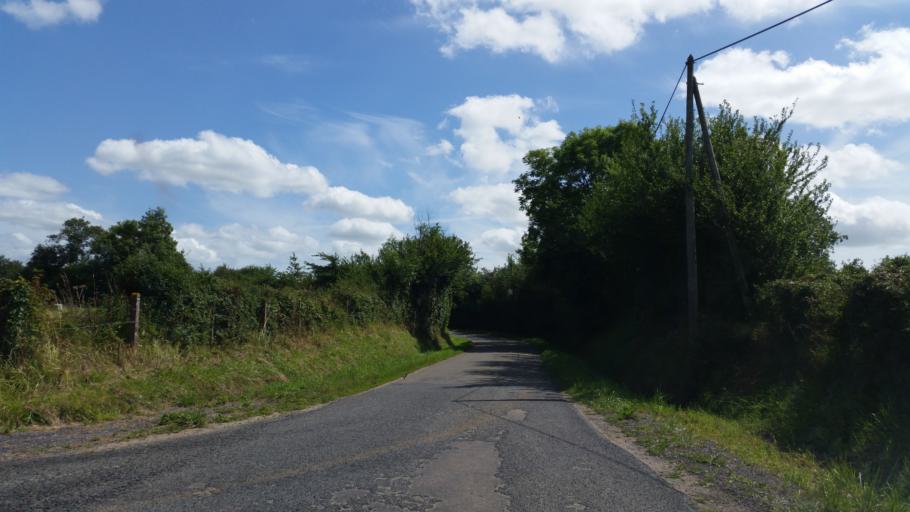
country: FR
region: Lower Normandy
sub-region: Departement de la Manche
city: Sainte-Mere-Eglise
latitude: 49.4625
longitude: -1.3315
